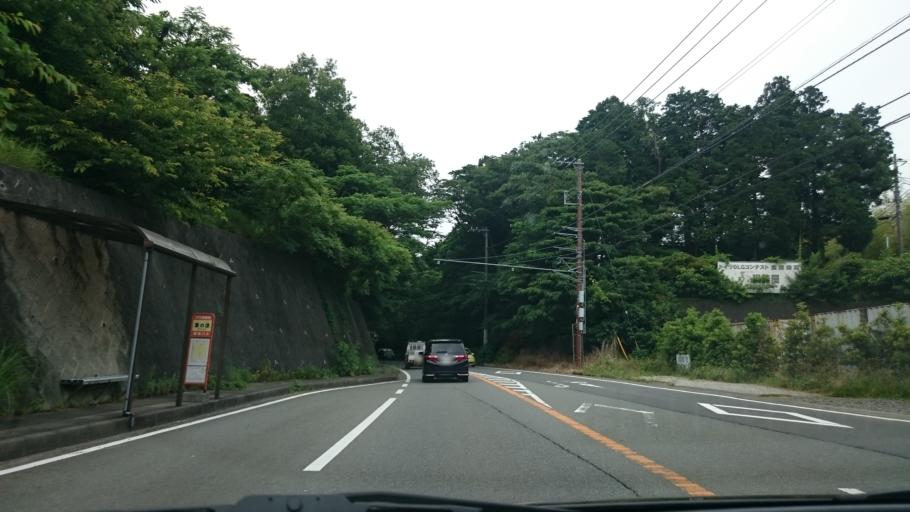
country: JP
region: Shizuoka
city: Ito
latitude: 34.9158
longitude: 139.1206
